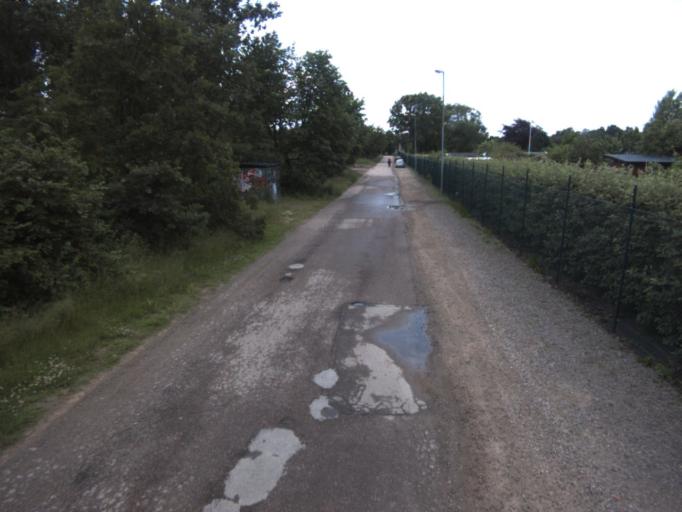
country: SE
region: Skane
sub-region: Helsingborg
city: Helsingborg
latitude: 56.0556
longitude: 12.7302
